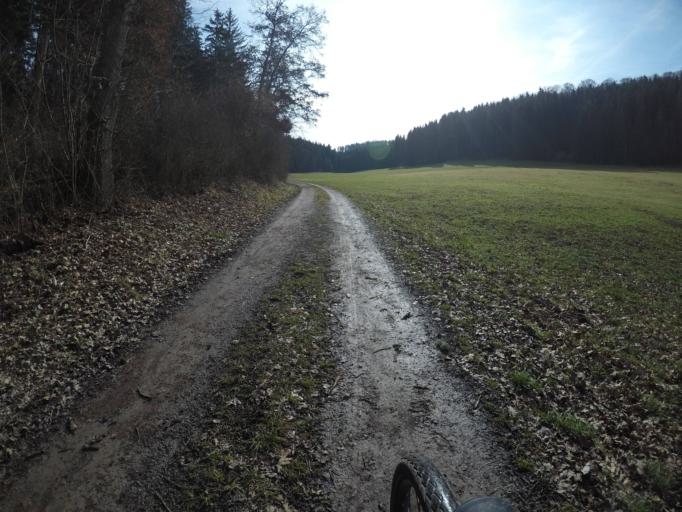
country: DE
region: Baden-Wuerttemberg
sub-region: Regierungsbezirk Stuttgart
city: Oberjettingen
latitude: 48.6007
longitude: 8.7888
